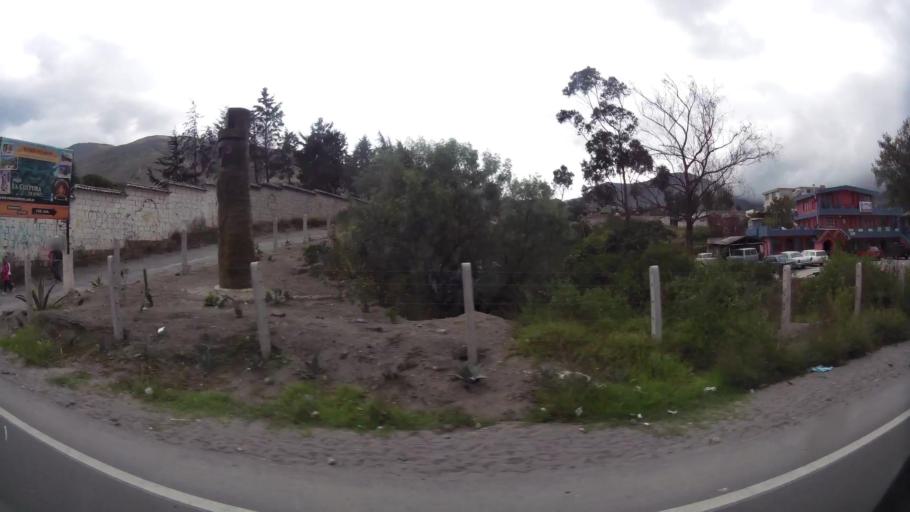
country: EC
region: Pichincha
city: Quito
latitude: -0.0014
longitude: -78.4529
